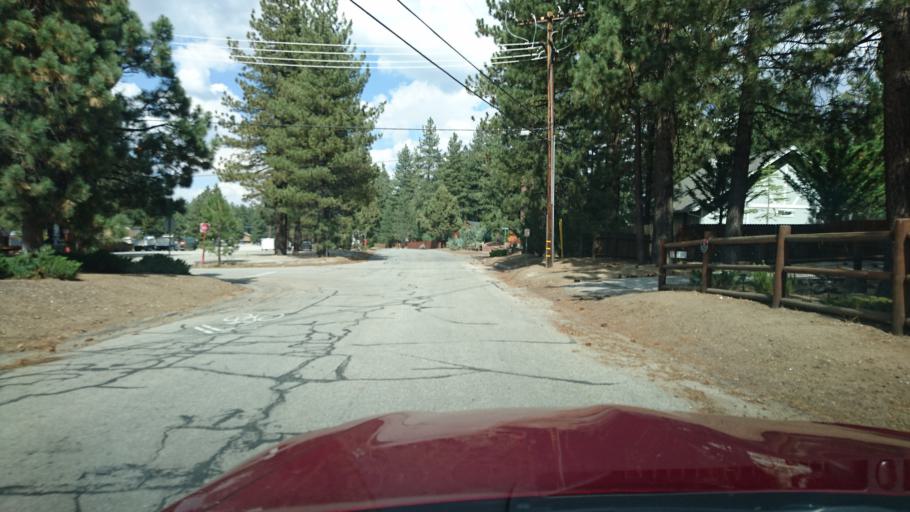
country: US
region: California
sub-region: San Bernardino County
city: Big Bear Lake
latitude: 34.2424
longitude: -116.8861
